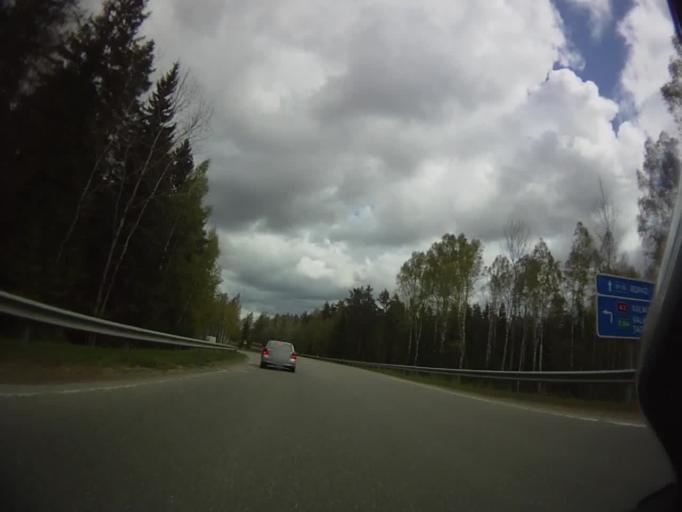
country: LV
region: Seja
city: Loja
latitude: 57.1155
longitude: 24.6370
